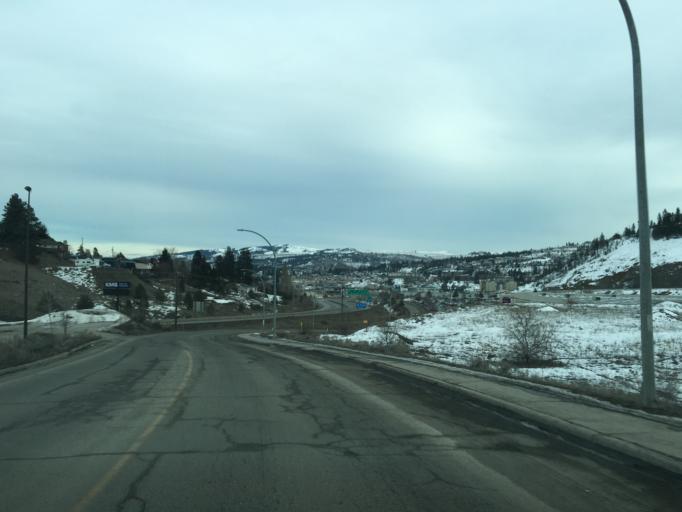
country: CA
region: British Columbia
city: Kamloops
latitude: 50.6568
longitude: -120.3923
